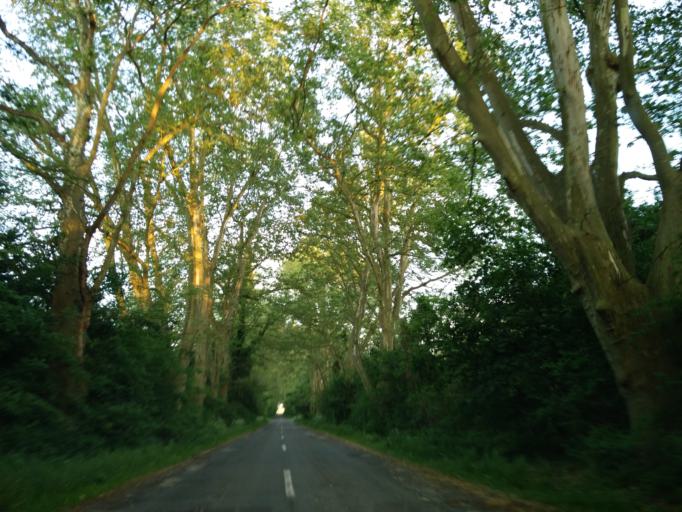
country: HU
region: Fejer
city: Bicske
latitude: 47.4367
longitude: 18.6141
